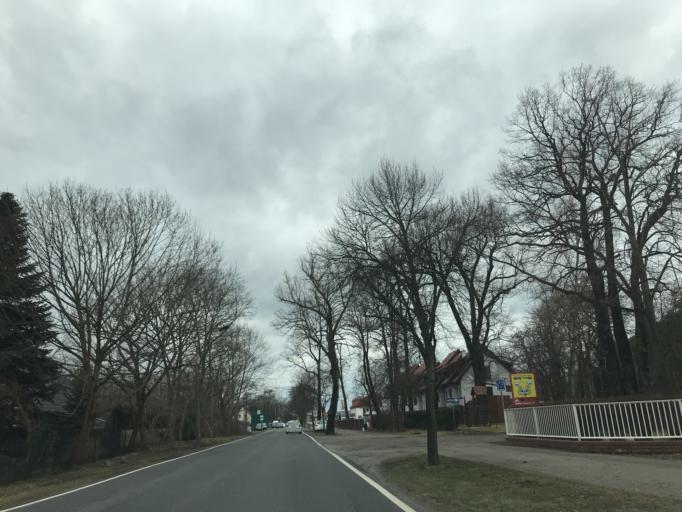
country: DE
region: Brandenburg
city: Luebben
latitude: 51.9460
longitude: 13.8830
